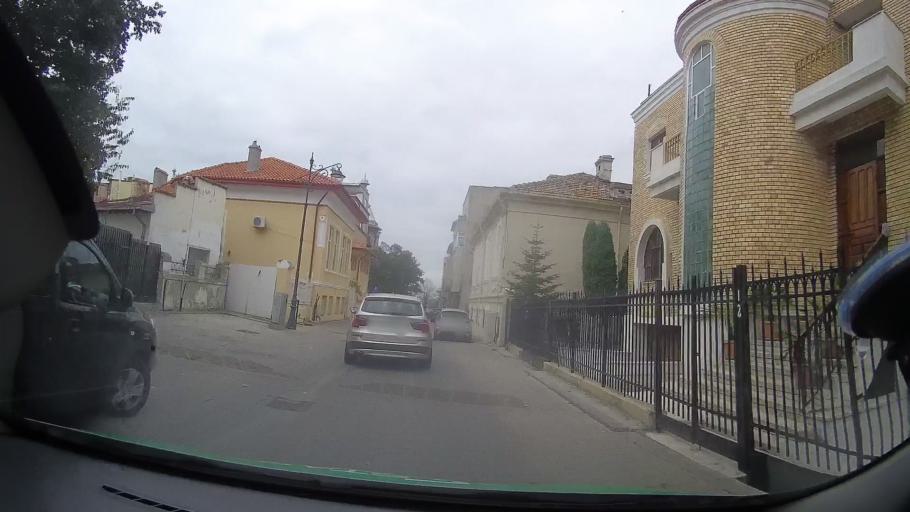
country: RO
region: Constanta
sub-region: Municipiul Constanta
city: Constanta
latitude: 44.1725
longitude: 28.6602
